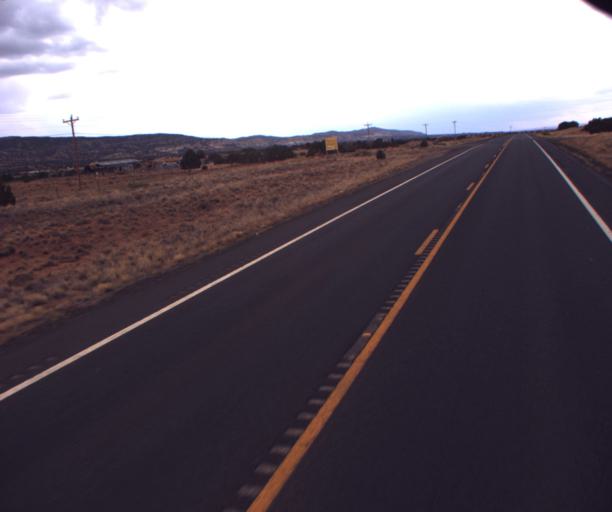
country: US
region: Arizona
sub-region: Coconino County
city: Kaibito
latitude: 36.4429
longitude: -110.7354
